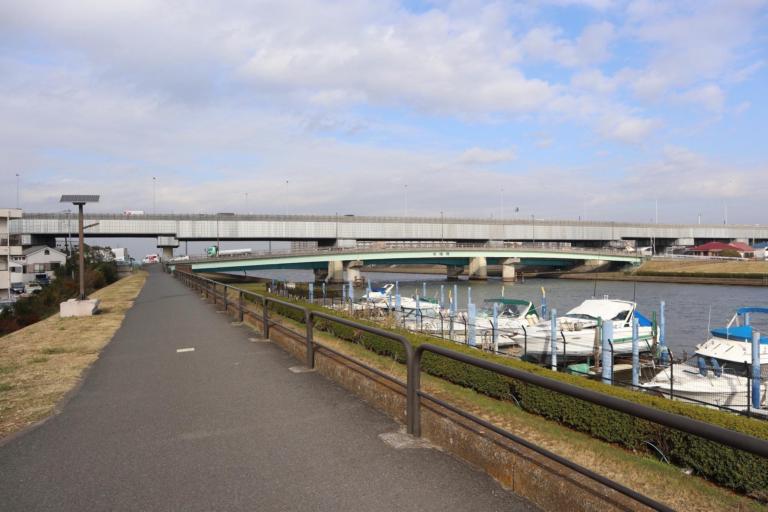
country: JP
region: Tokyo
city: Urayasu
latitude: 35.6963
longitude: 139.8850
